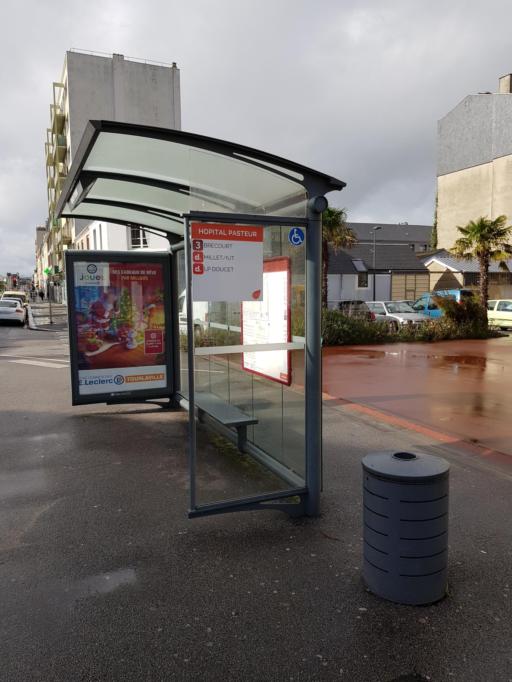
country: FR
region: Lower Normandy
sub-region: Departement de la Manche
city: Cherbourg-Octeville
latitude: 49.6386
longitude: -1.6132
